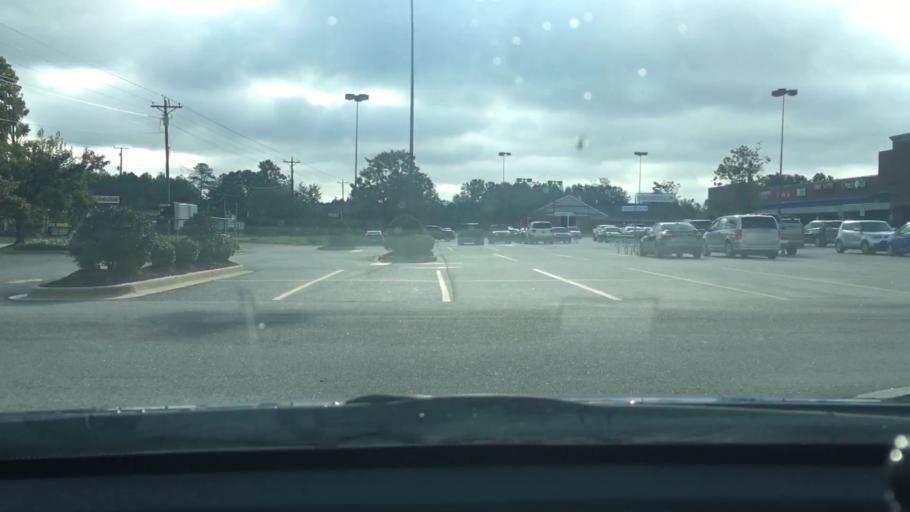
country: US
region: South Carolina
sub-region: Lexington County
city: Irmo
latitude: 34.0955
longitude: -81.1594
